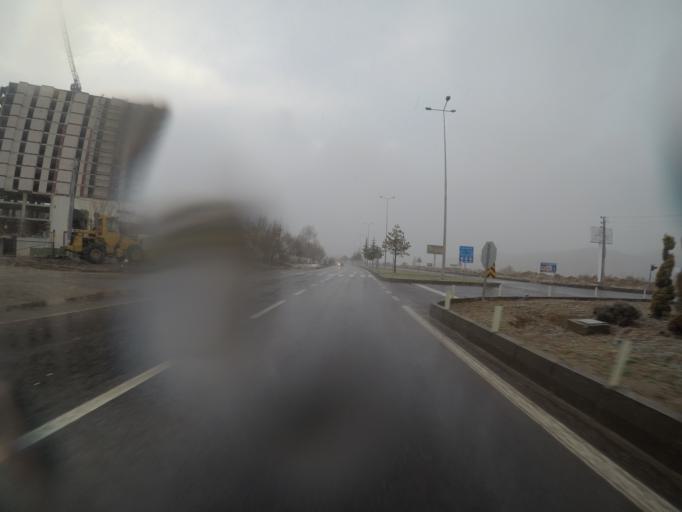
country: TR
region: Nevsehir
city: Nevsehir
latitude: 38.6317
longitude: 34.7536
